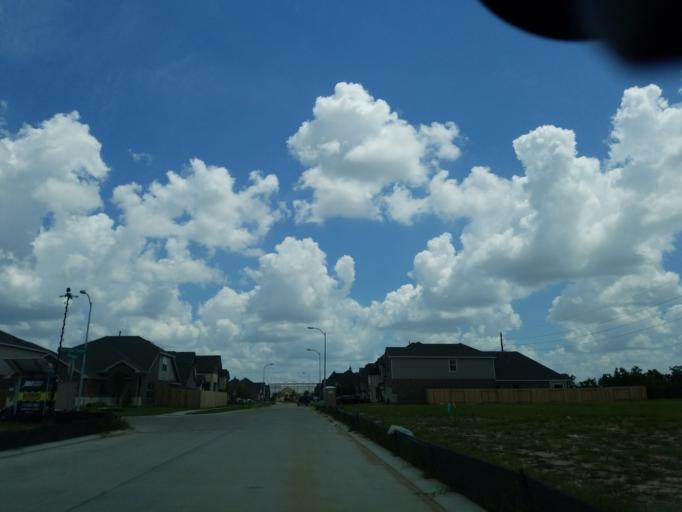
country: US
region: Texas
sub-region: Harris County
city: Katy
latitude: 29.8304
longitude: -95.7812
